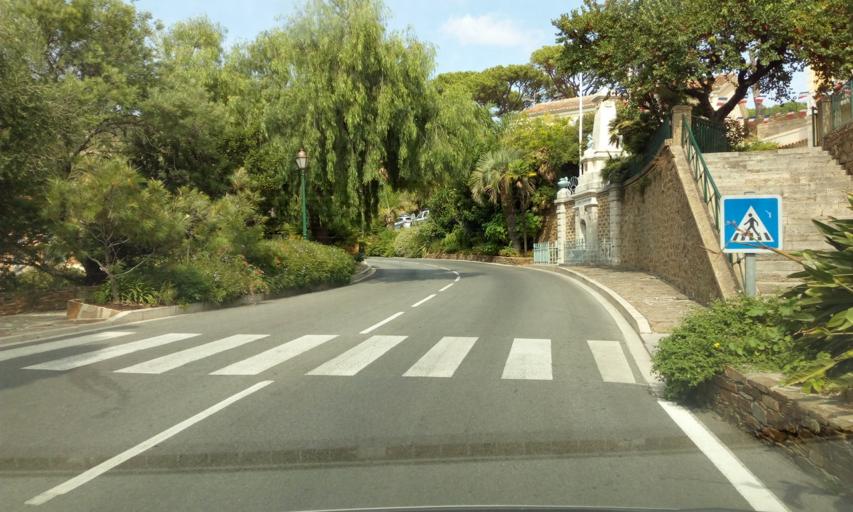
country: FR
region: Provence-Alpes-Cote d'Azur
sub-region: Departement du Var
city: Bormes-les-Mimosas
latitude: 43.1503
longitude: 6.3437
